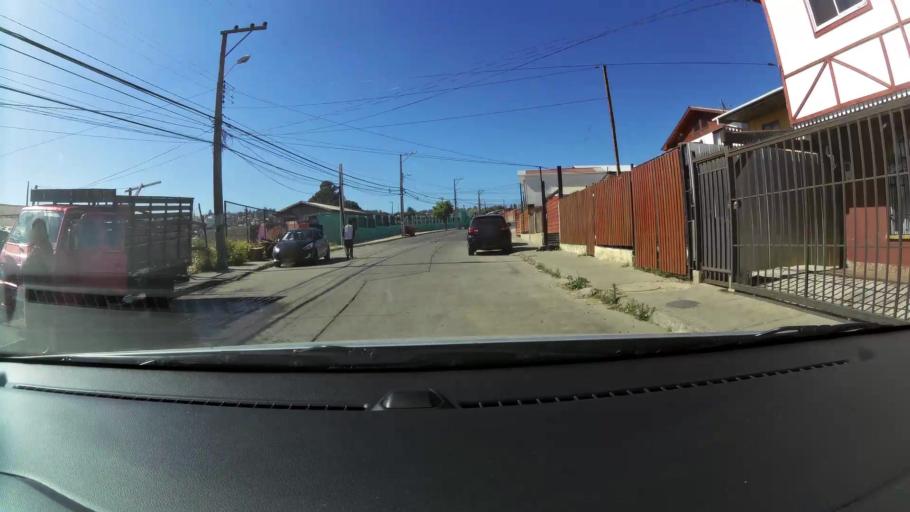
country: CL
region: Valparaiso
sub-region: Provincia de Valparaiso
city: Valparaiso
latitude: -33.0534
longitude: -71.6443
